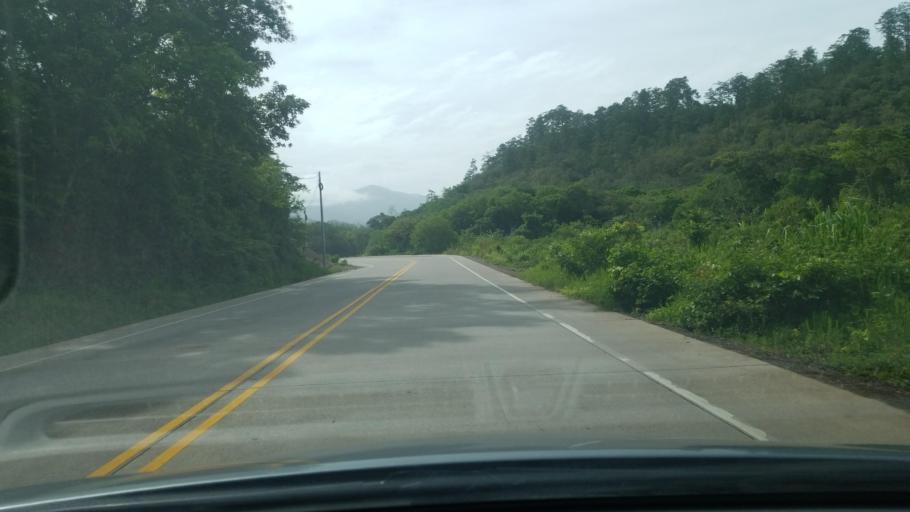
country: HN
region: Copan
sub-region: Santa Rita
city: Santa Rita, Copan
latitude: 14.8696
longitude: -89.0735
